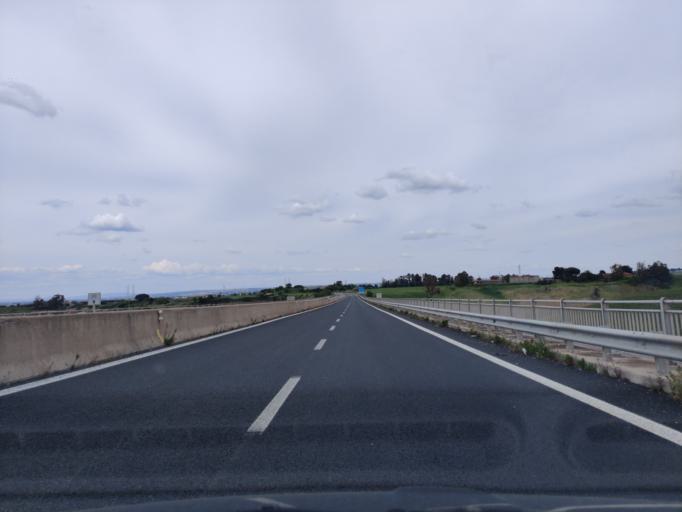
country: IT
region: Latium
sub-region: Citta metropolitana di Roma Capitale
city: Aurelia
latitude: 42.1477
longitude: 11.7915
